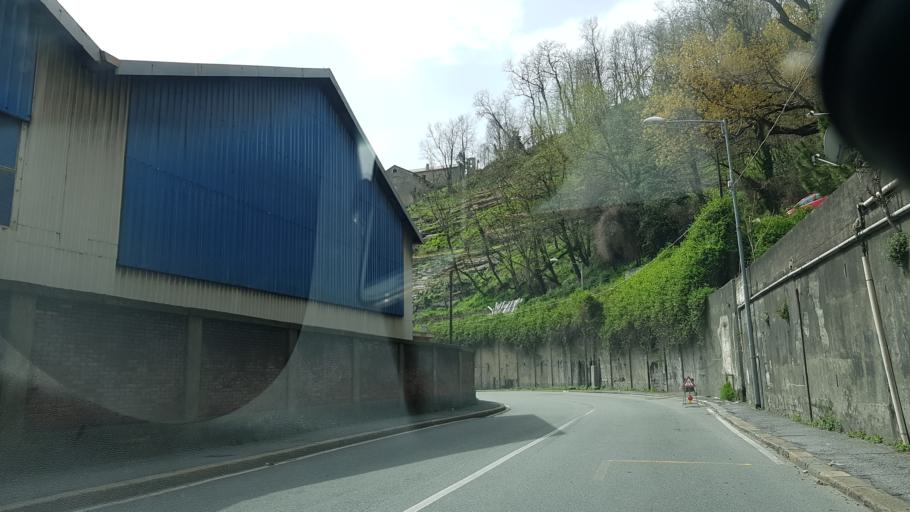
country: IT
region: Liguria
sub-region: Provincia di Genova
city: San Teodoro
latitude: 44.4270
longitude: 8.8819
